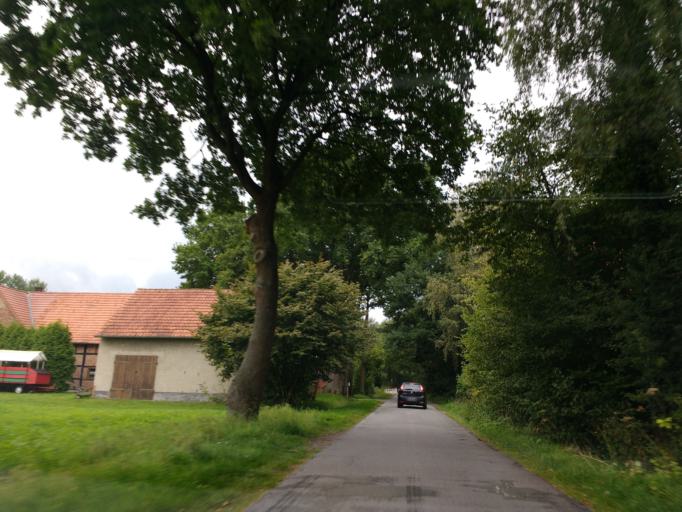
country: DE
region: North Rhine-Westphalia
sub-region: Regierungsbezirk Detmold
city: Hovelhof
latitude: 51.7725
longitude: 8.6609
